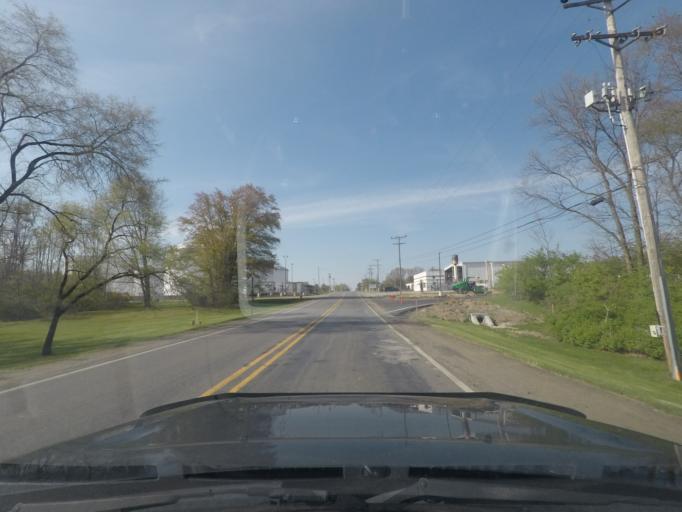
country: US
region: Michigan
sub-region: Berrien County
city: Niles
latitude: 41.7844
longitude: -86.2548
